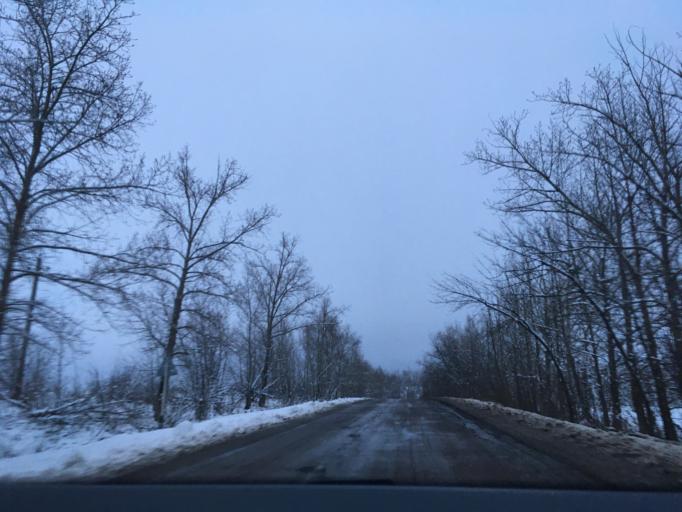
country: RU
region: Voronezj
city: Verkhniy Mamon
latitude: 50.0560
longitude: 40.2535
